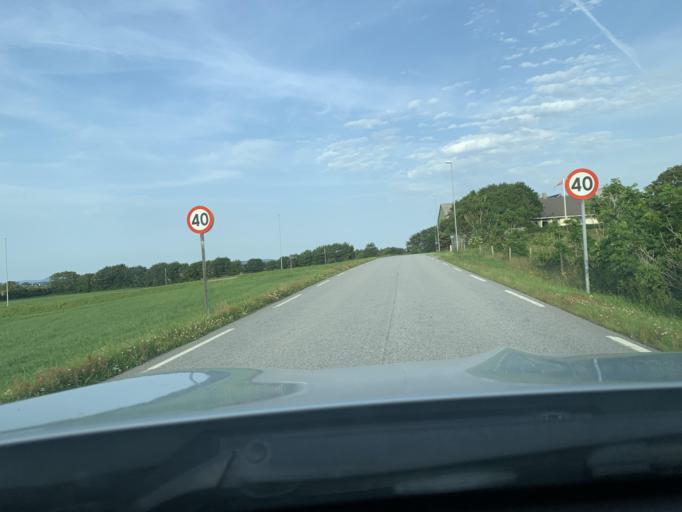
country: NO
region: Rogaland
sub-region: Klepp
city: Kleppe
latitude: 58.7190
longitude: 5.5624
